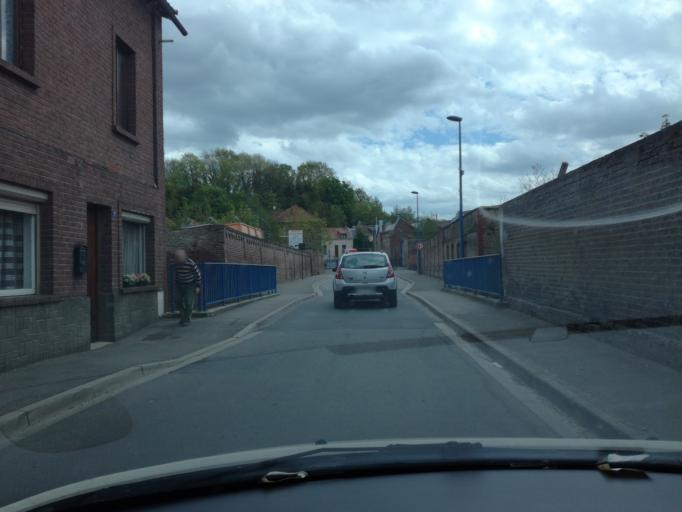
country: FR
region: Picardie
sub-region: Departement de la Somme
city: Saleux
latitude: 49.8565
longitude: 2.2379
